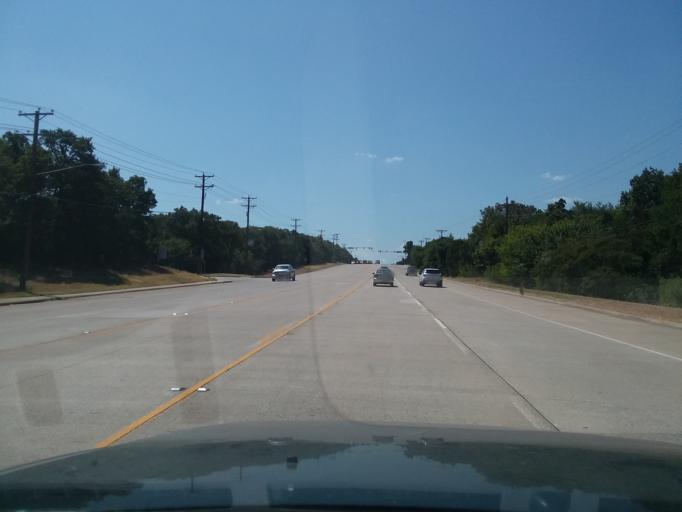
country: US
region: Texas
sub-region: Tarrant County
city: Euless
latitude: 32.8614
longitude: -97.1001
